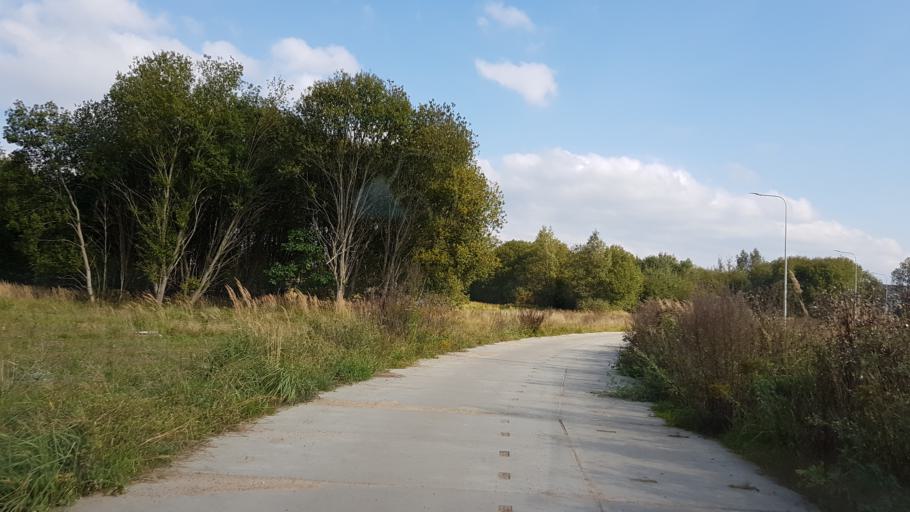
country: PL
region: West Pomeranian Voivodeship
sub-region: Koszalin
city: Koszalin
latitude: 54.1795
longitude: 16.1613
